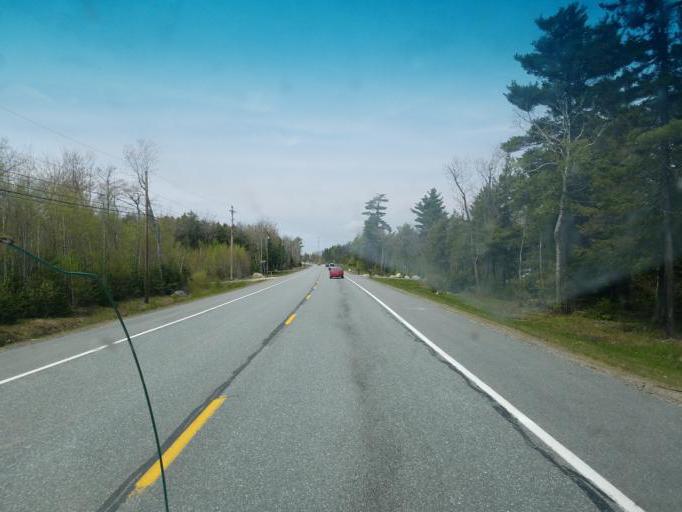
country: US
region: Maine
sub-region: Hancock County
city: Surry
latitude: 44.6088
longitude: -68.5194
